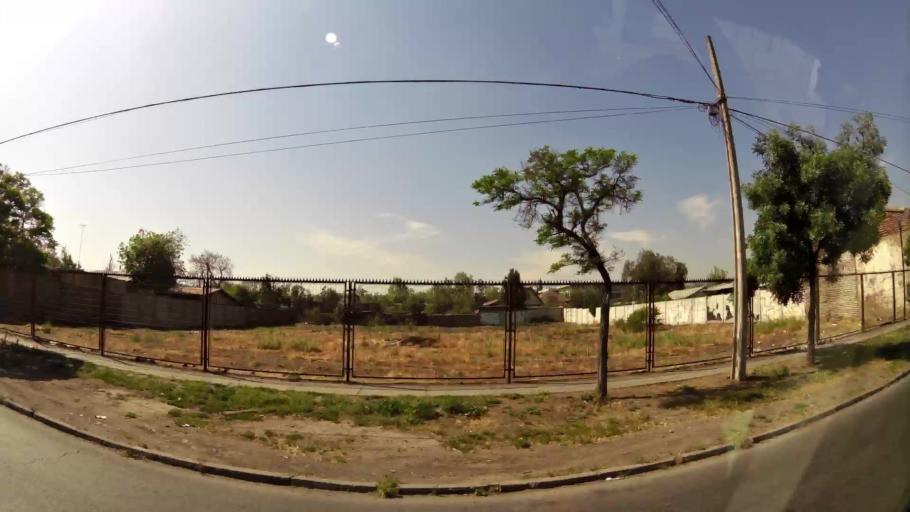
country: CL
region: Santiago Metropolitan
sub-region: Provincia de Maipo
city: San Bernardo
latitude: -33.5860
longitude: -70.7044
